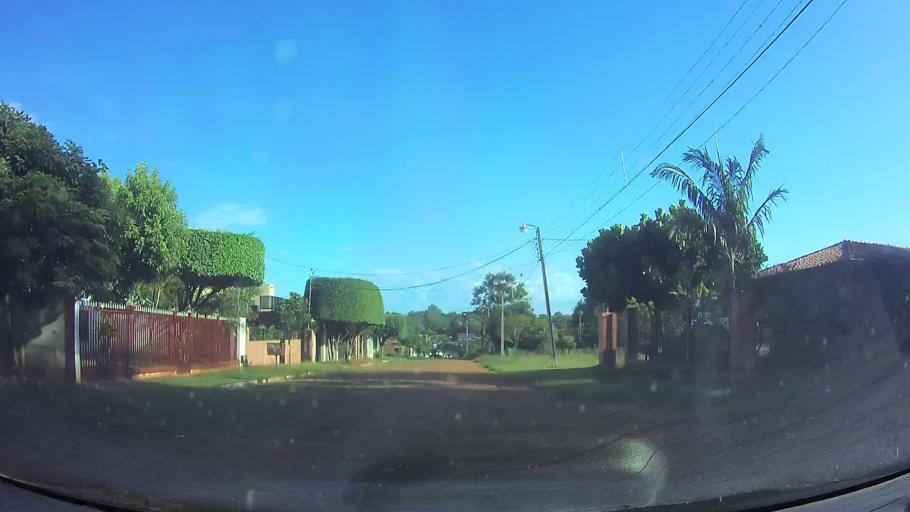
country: PY
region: Central
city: Limpio
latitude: -25.2557
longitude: -57.4684
